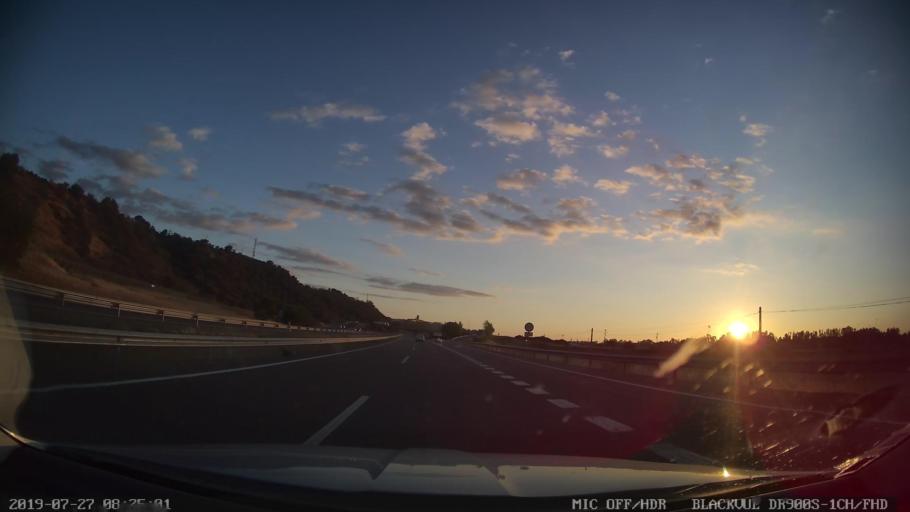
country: ES
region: Extremadura
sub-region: Provincia de Badajoz
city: Lobon
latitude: 38.8553
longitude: -6.6034
